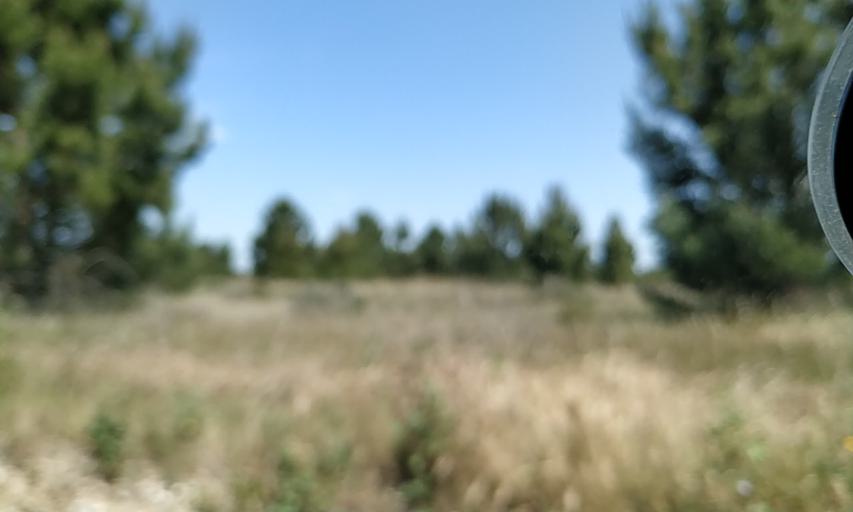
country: PT
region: Setubal
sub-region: Palmela
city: Palmela
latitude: 38.6249
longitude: -8.7466
